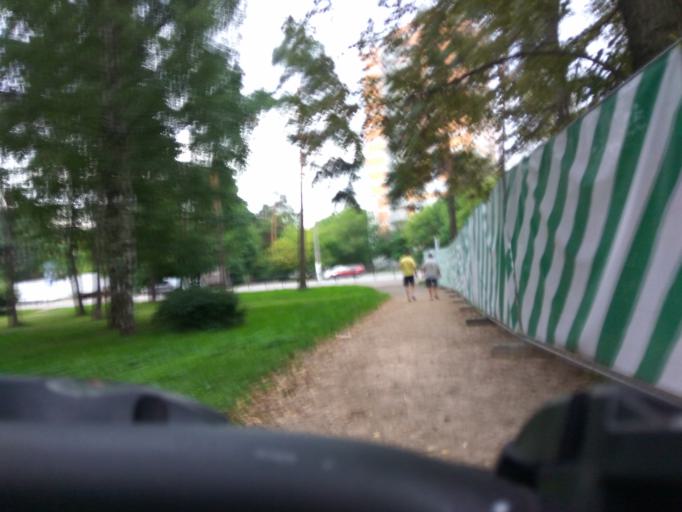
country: RU
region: Moscow
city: Tsaritsyno
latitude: 55.6263
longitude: 37.6597
